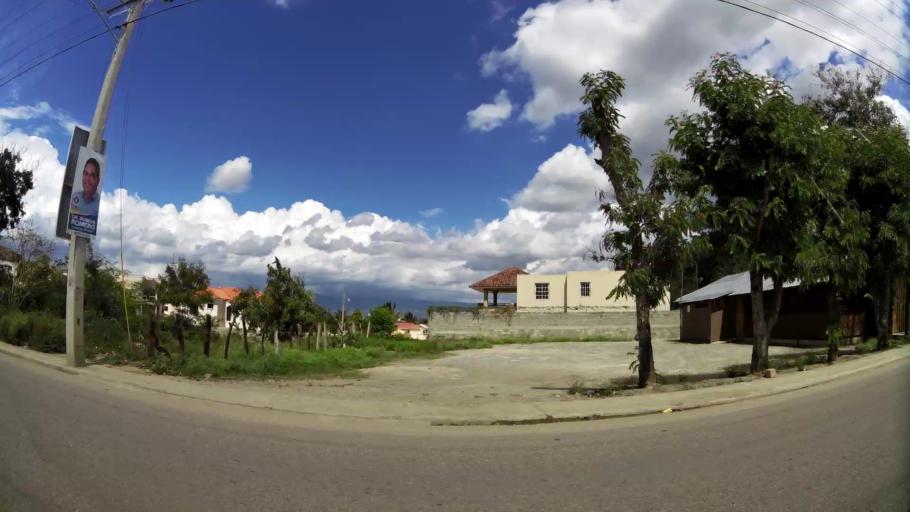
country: DO
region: Santiago
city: Santiago de los Caballeros
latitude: 19.4167
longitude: -70.6782
